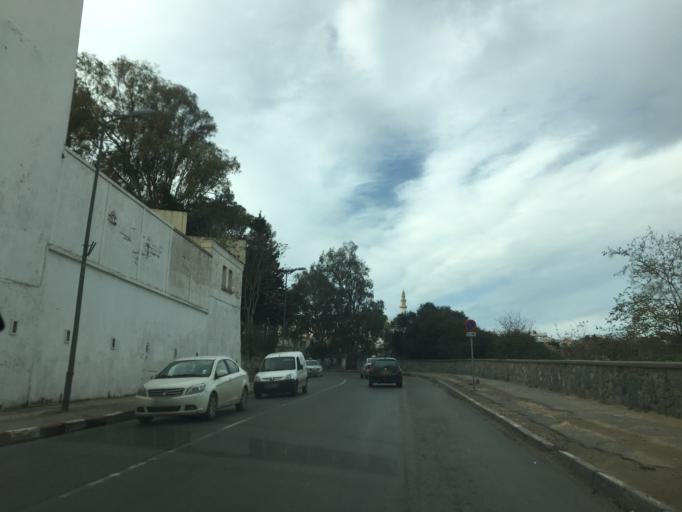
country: DZ
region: Alger
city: Algiers
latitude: 36.7761
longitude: 3.0471
